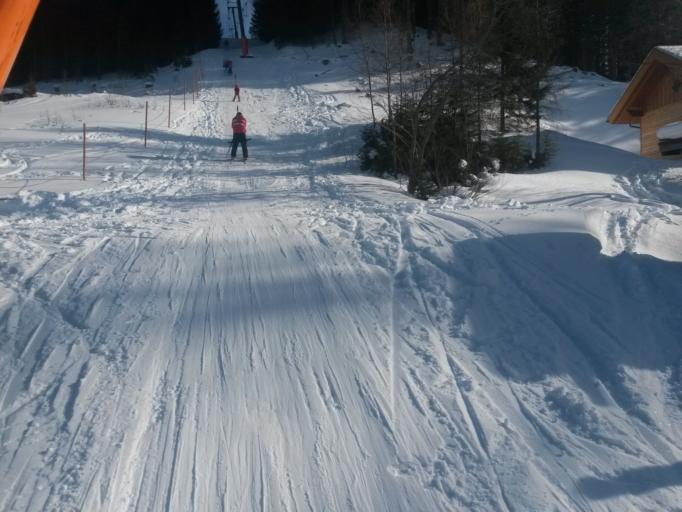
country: AT
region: Salzburg
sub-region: Politischer Bezirk Sankt Johann im Pongau
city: Dorfgastein
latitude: 47.2410
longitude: 13.1239
